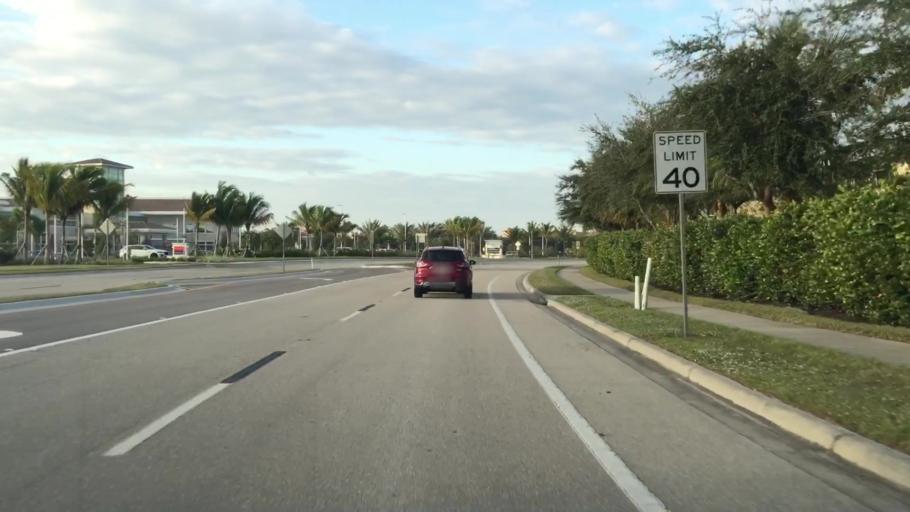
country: US
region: Florida
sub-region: Lee County
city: Estero
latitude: 26.3946
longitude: -81.8056
